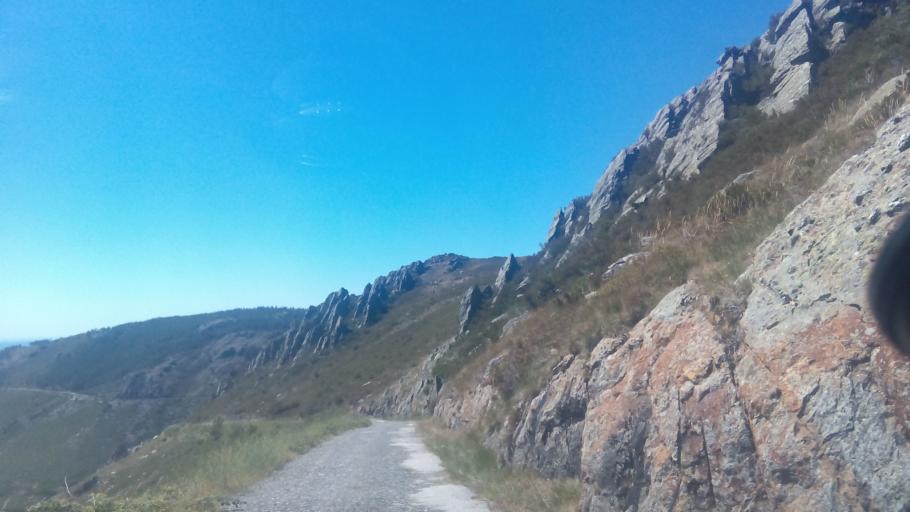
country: PT
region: Vila Real
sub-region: Mesao Frio
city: Mesao Frio
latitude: 41.2663
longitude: -7.9036
